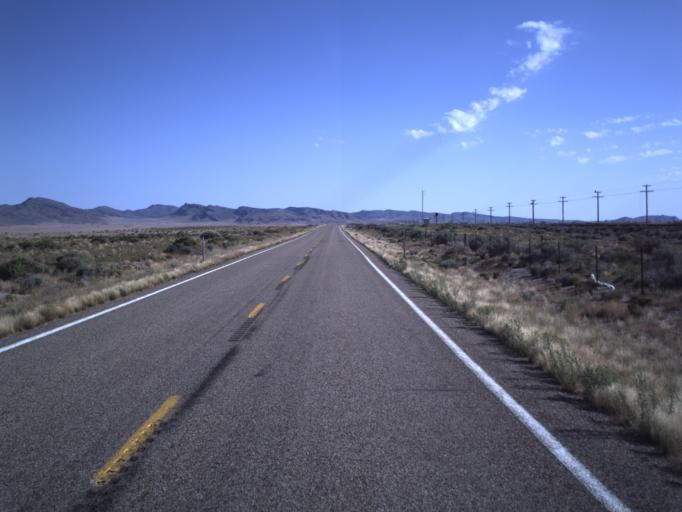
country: US
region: Utah
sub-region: Beaver County
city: Milford
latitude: 38.6574
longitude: -112.9818
